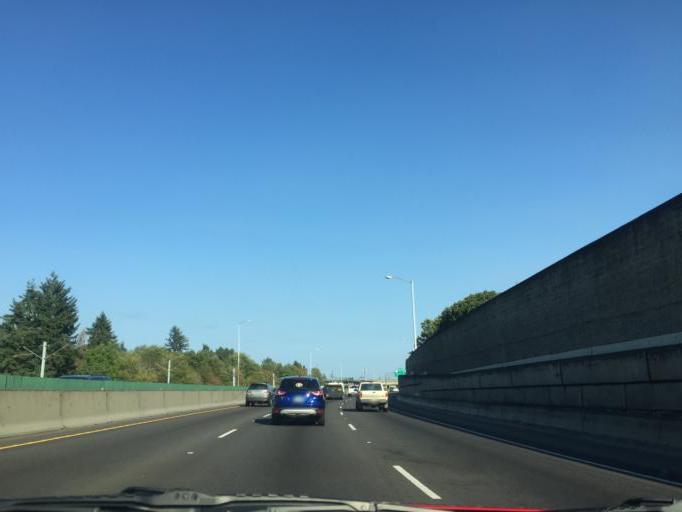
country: US
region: Oregon
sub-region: Multnomah County
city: Lents
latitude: 45.5355
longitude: -122.5851
